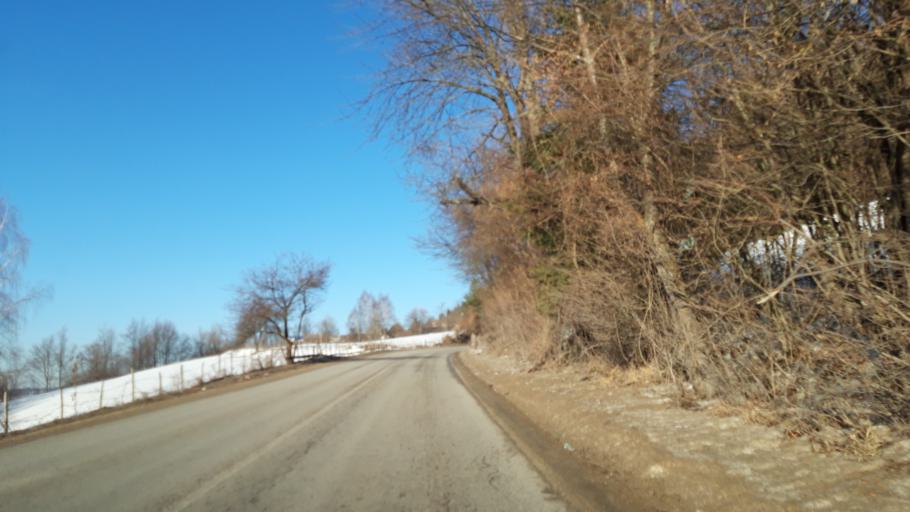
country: BA
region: Republika Srpska
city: Pale
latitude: 43.8987
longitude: 18.6355
